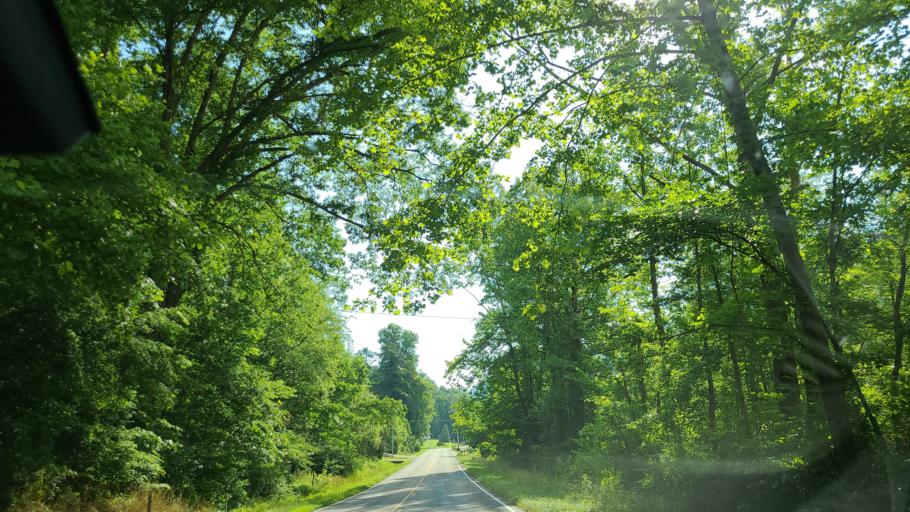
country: US
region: Kentucky
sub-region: Bell County
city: Pineville
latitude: 36.7075
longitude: -83.8357
